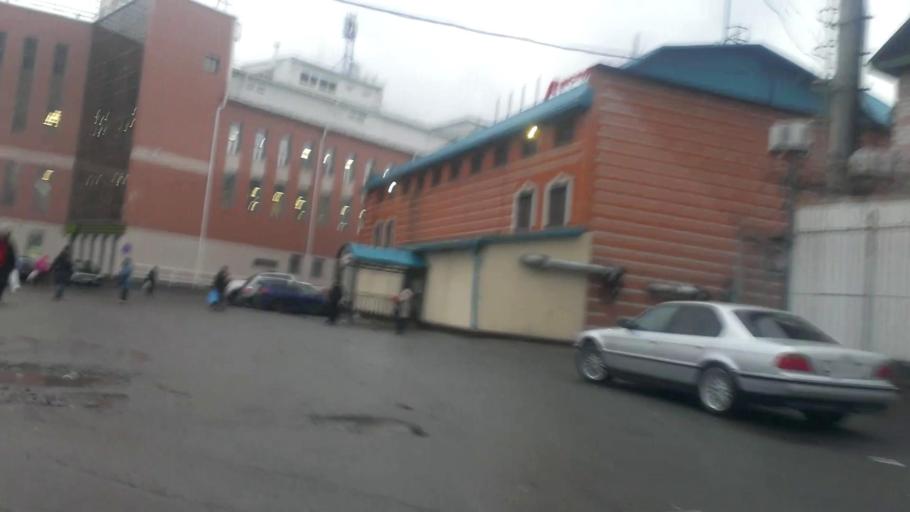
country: RU
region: Altai Krai
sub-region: Gorod Barnaulskiy
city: Barnaul
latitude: 53.3583
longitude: 83.6981
